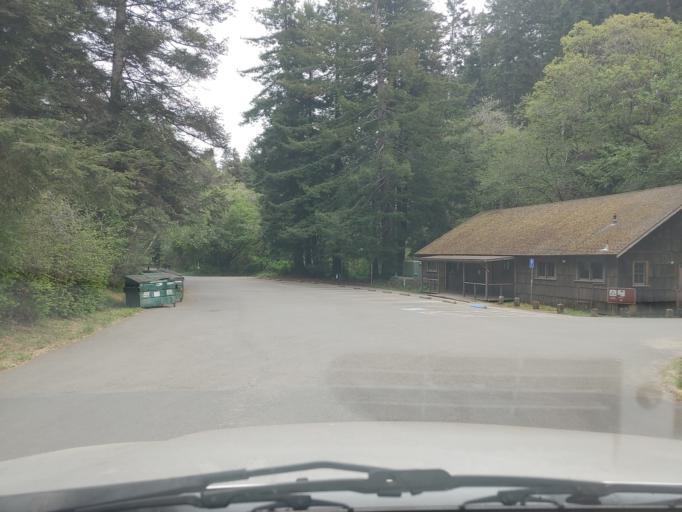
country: US
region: California
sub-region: Mendocino County
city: Fort Bragg
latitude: 39.3305
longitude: -123.8023
